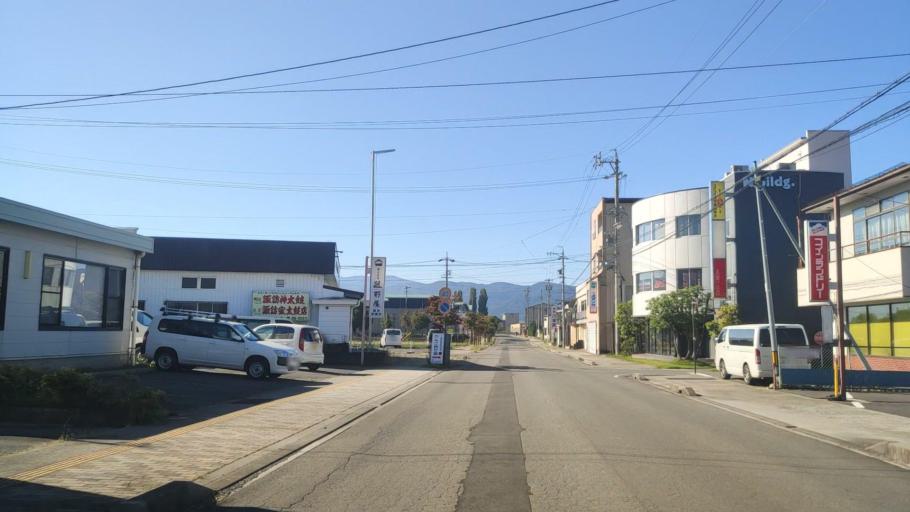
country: JP
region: Nagano
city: Okaya
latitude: 36.0648
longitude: 138.0801
